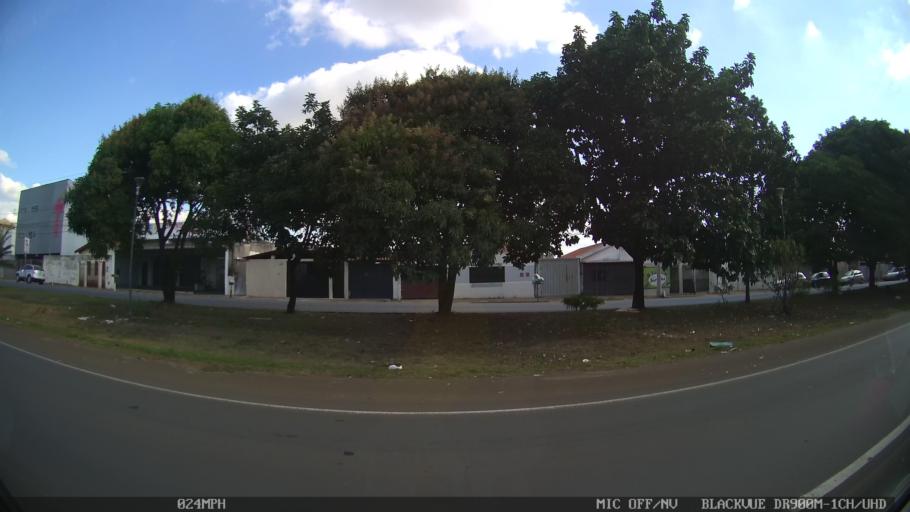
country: BR
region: Sao Paulo
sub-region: Santa Barbara D'Oeste
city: Santa Barbara d'Oeste
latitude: -22.7678
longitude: -47.3878
